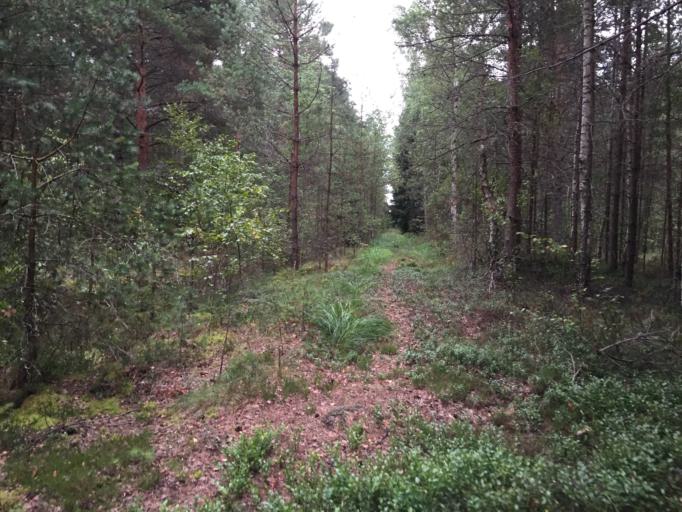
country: LV
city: Tireli
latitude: 56.8505
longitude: 23.6727
